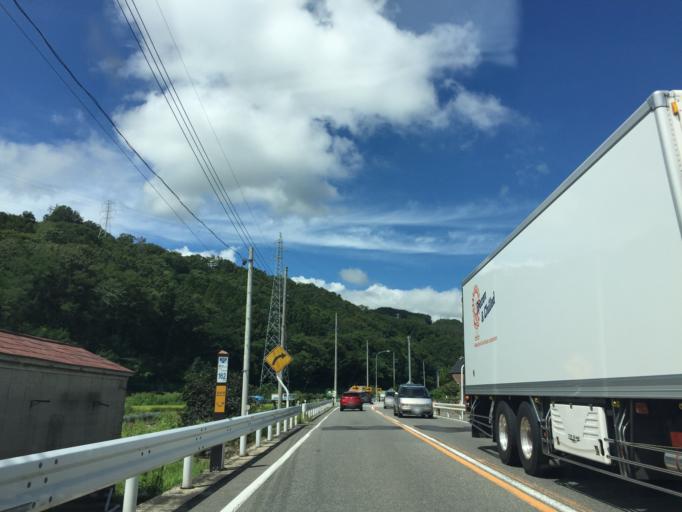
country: JP
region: Yamanashi
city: Nirasaki
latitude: 35.7964
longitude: 138.3636
